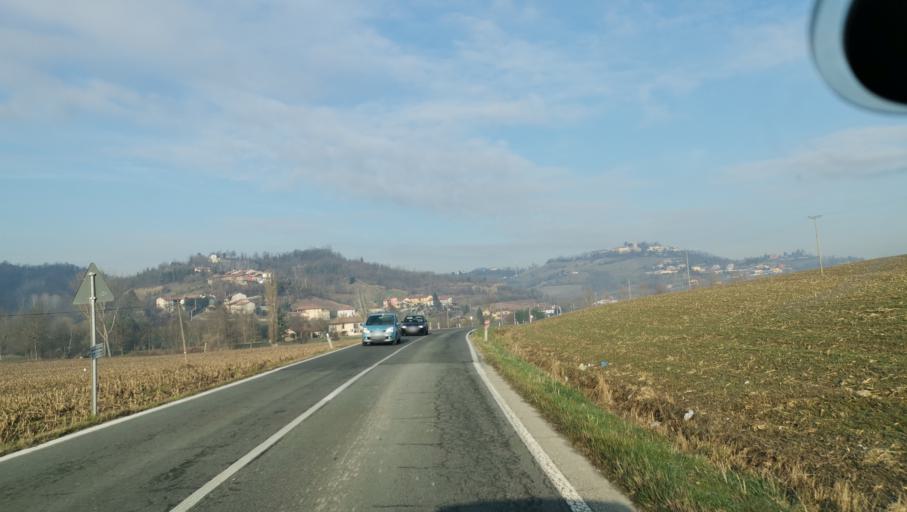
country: IT
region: Piedmont
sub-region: Provincia di Torino
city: Casalborgone
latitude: 45.1406
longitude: 7.9382
